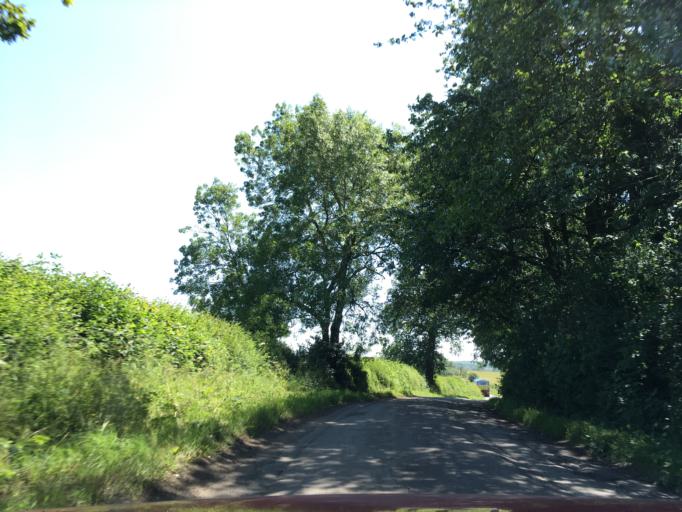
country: GB
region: England
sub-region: Northamptonshire
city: Deanshanger
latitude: 52.0060
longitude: -0.8868
